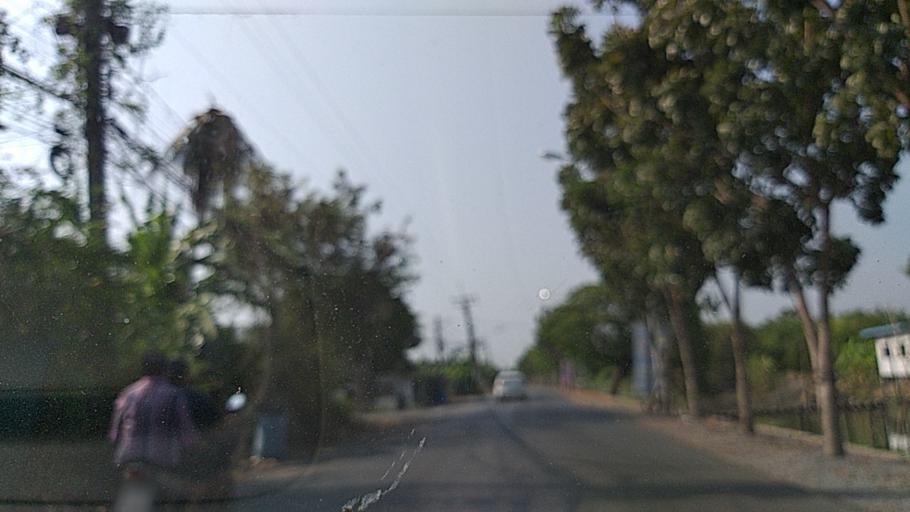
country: TH
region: Pathum Thani
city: Lam Luk Ka
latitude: 13.9558
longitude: 100.7057
